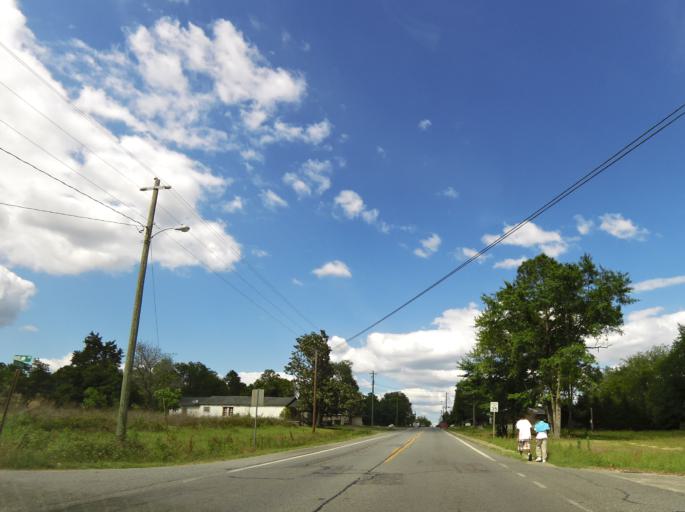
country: US
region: Georgia
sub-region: Treutlen County
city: Soperton
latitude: 32.3745
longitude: -82.6008
